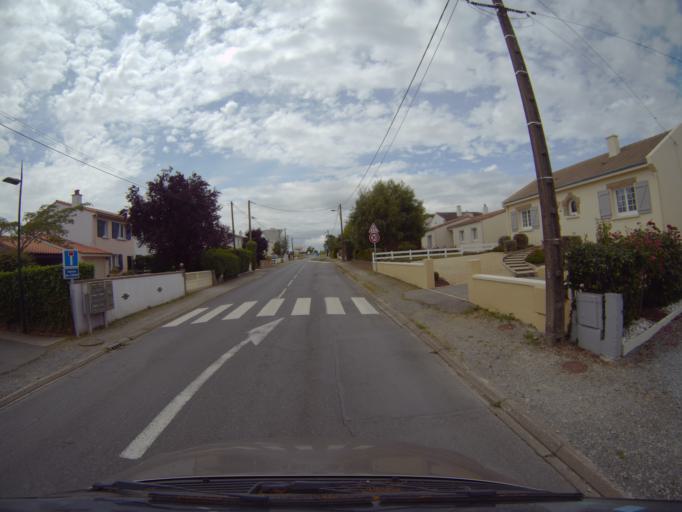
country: FR
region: Pays de la Loire
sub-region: Departement de la Loire-Atlantique
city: Montbert
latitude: 47.0582
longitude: -1.4930
